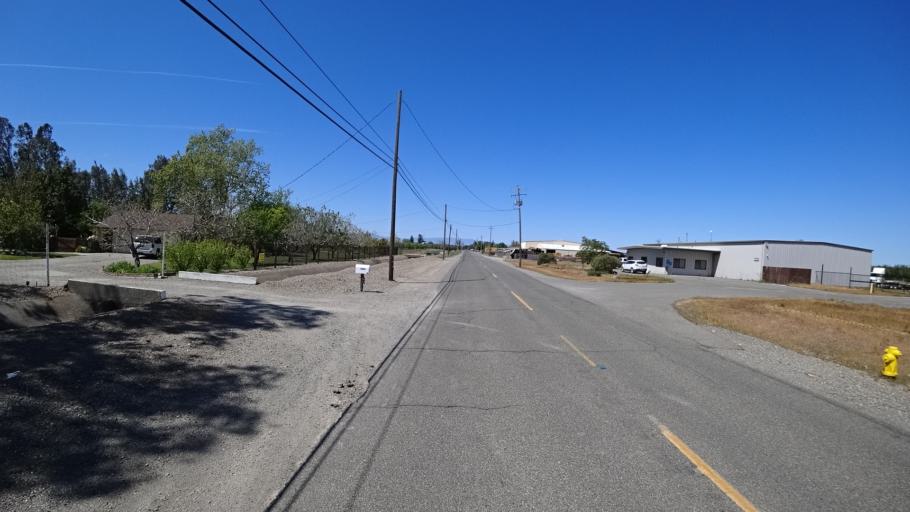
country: US
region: California
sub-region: Glenn County
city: Orland
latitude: 39.7340
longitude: -122.1630
